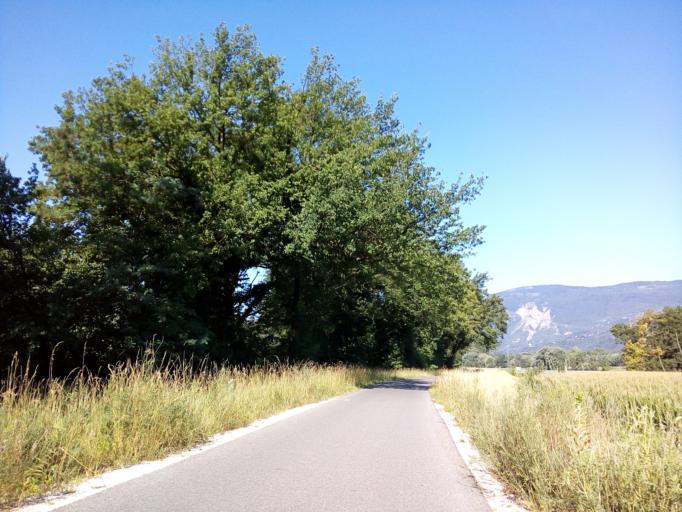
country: FR
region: Rhone-Alpes
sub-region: Departement de l'Isere
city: Montbonnot-Saint-Martin
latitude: 45.2069
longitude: 5.8077
